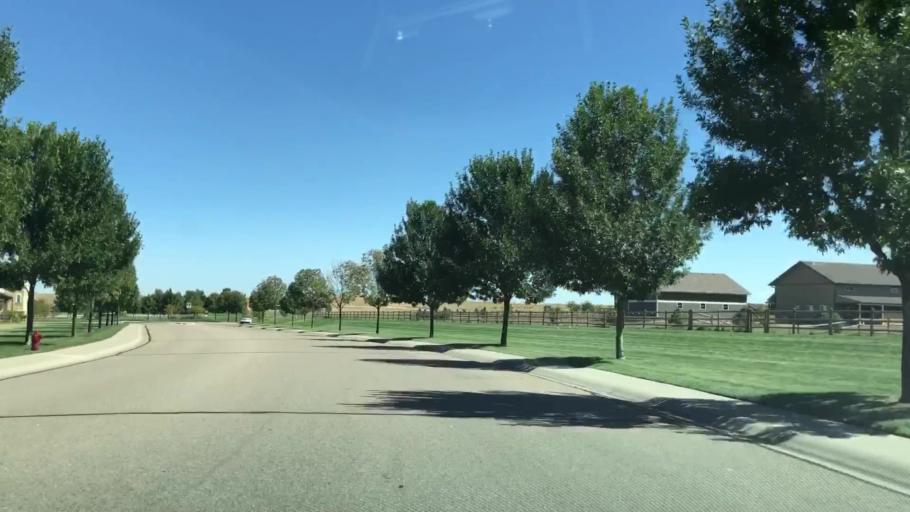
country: US
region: Colorado
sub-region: Weld County
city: Windsor
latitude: 40.4507
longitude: -104.9500
